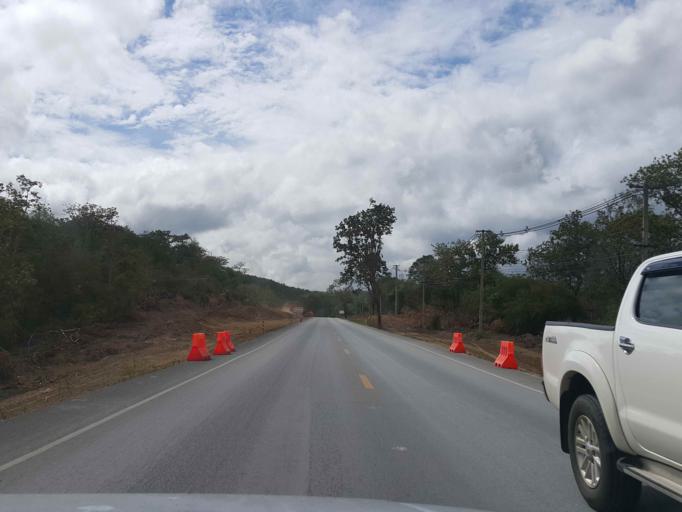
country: TH
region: Tak
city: Tak
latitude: 16.7993
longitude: 99.0053
